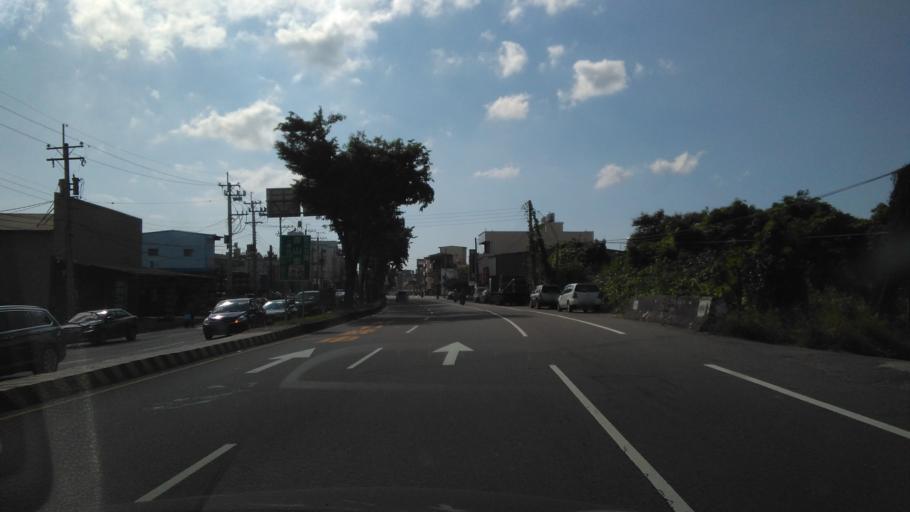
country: TW
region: Taiwan
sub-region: Changhua
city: Chang-hua
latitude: 24.0828
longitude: 120.5942
